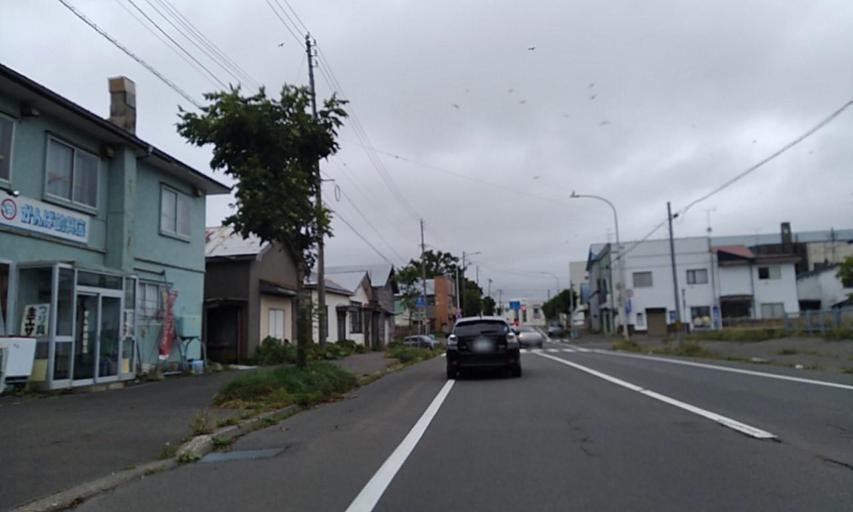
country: JP
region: Hokkaido
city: Nemuro
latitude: 43.3353
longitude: 145.5786
